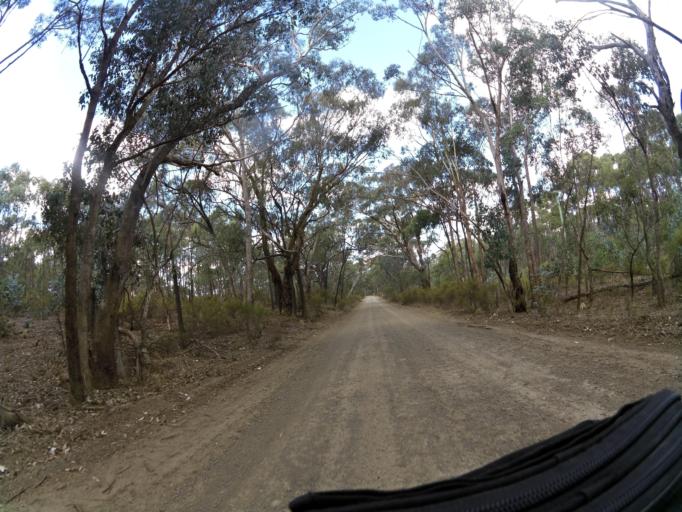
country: AU
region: Victoria
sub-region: Greater Bendigo
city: Kennington
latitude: -36.9625
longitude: 144.7800
